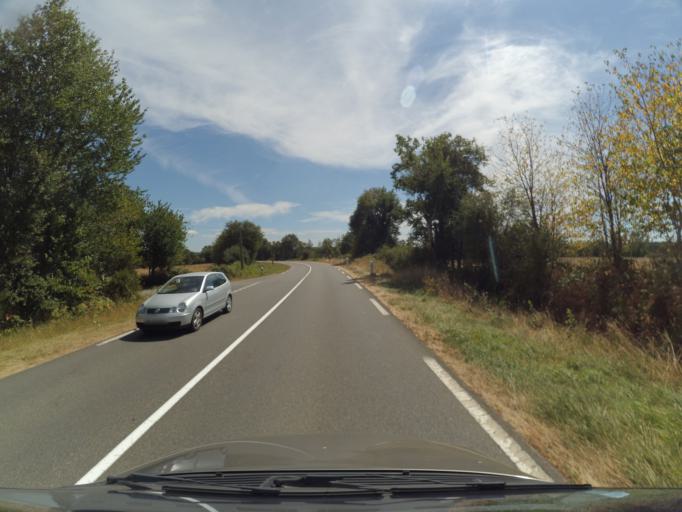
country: FR
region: Poitou-Charentes
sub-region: Departement de la Vienne
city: Availles-Limouzine
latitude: 46.0718
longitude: 0.5932
